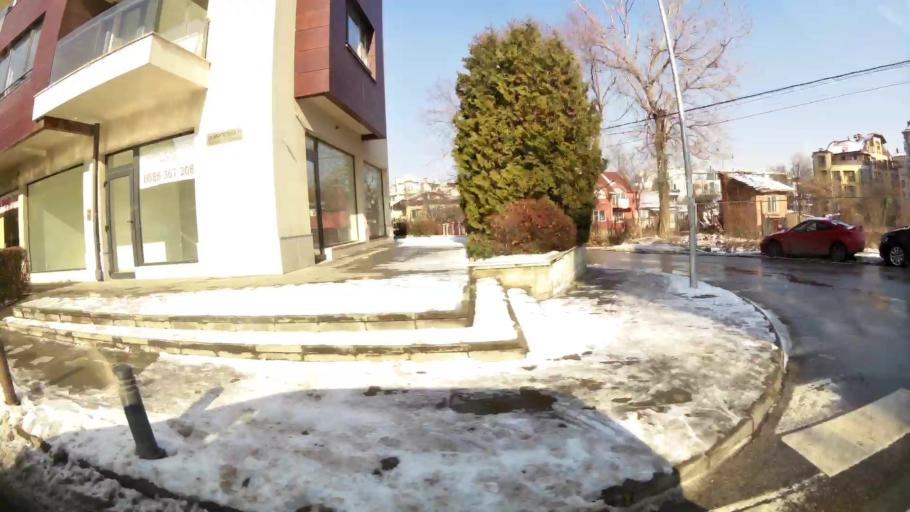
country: BG
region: Sofia-Capital
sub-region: Stolichna Obshtina
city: Sofia
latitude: 42.6532
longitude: 23.3330
